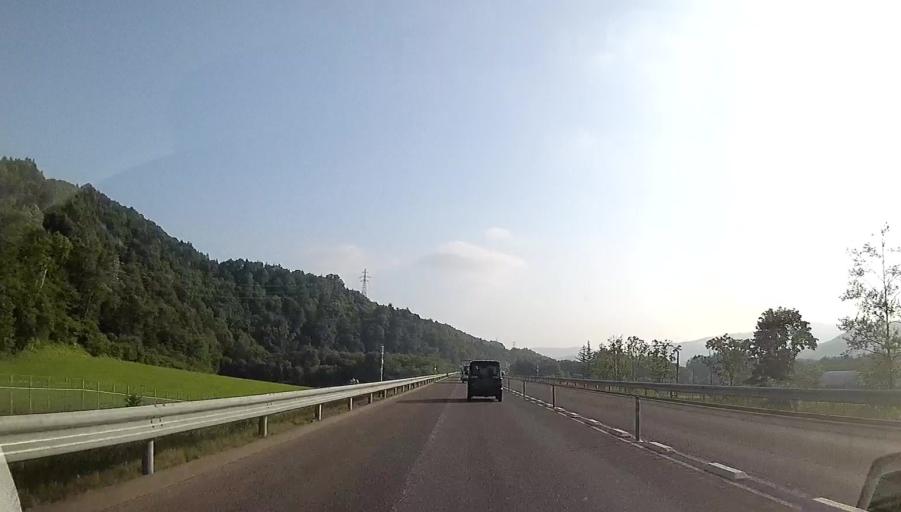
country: JP
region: Hokkaido
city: Shimo-furano
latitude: 43.0166
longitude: 142.4336
